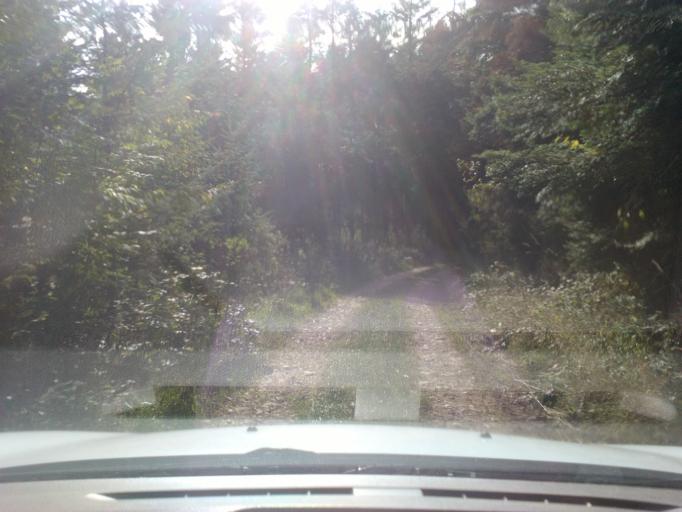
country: FR
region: Lorraine
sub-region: Departement des Vosges
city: Sainte-Marguerite
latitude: 48.3006
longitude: 7.0314
